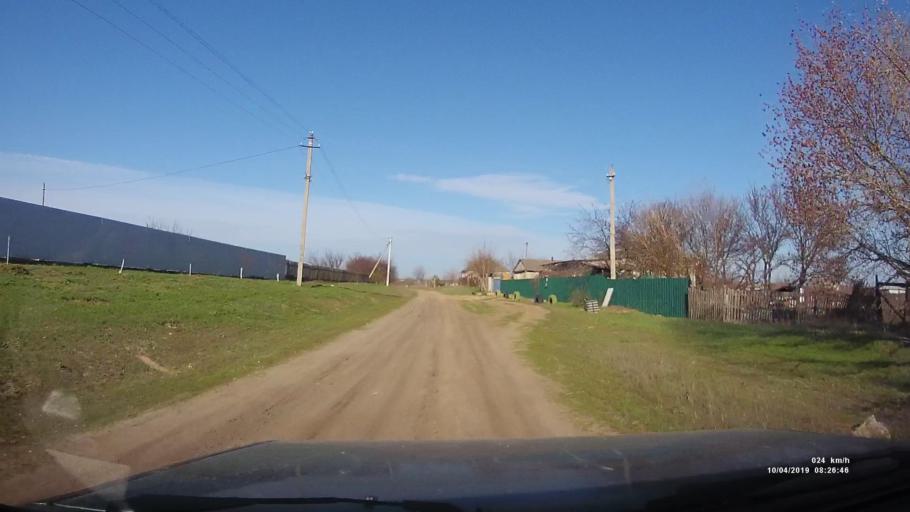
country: RU
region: Rostov
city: Kamensk-Shakhtinskiy
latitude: 48.3582
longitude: 40.2266
